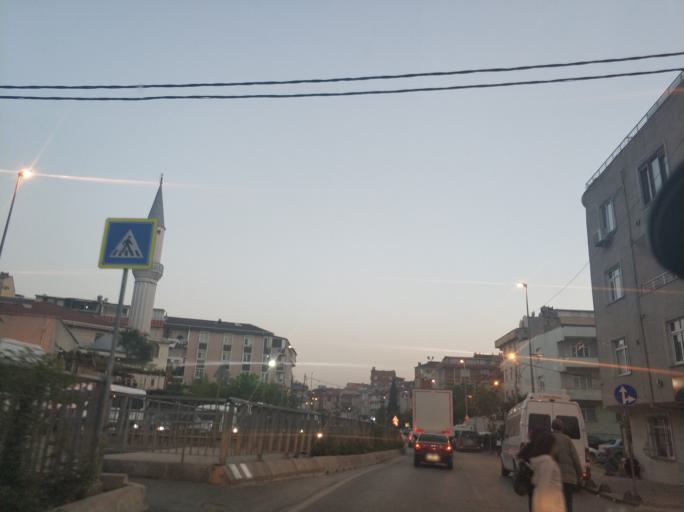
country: TR
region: Istanbul
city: Bagcilar
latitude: 41.0538
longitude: 28.8486
